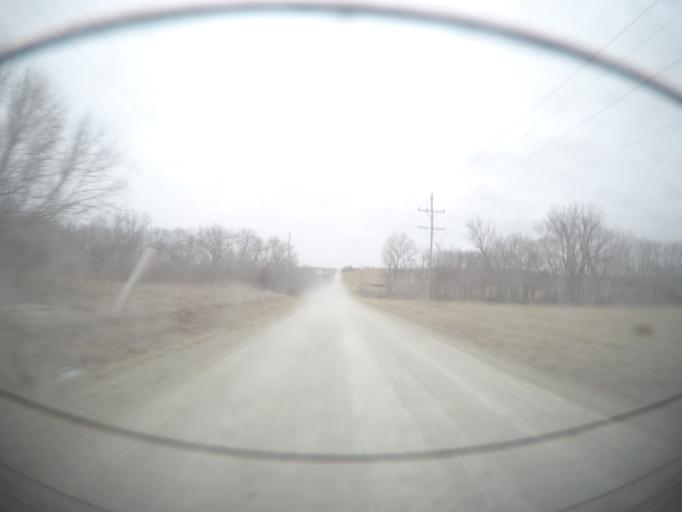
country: US
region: Kansas
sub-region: Wabaunsee County
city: Alma
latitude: 39.0813
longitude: -96.2424
